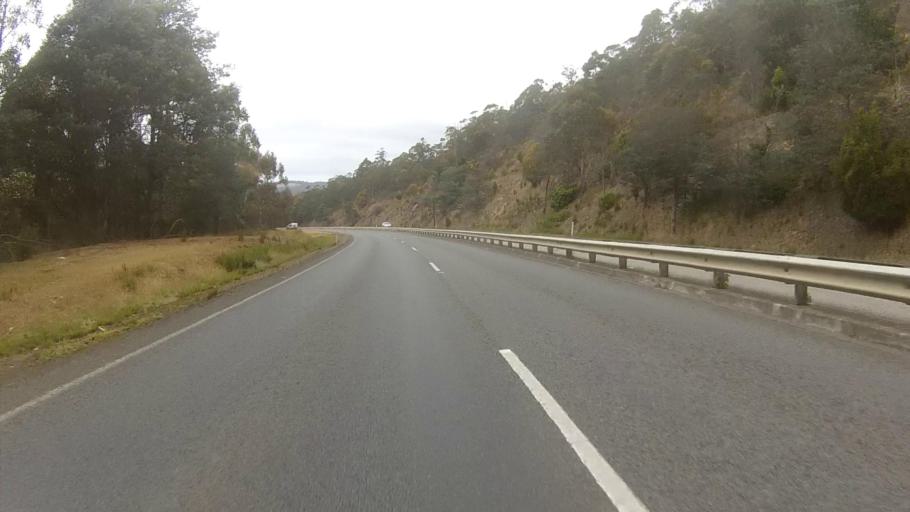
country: AU
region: Tasmania
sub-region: Kingborough
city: Margate
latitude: -42.9839
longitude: 147.1790
